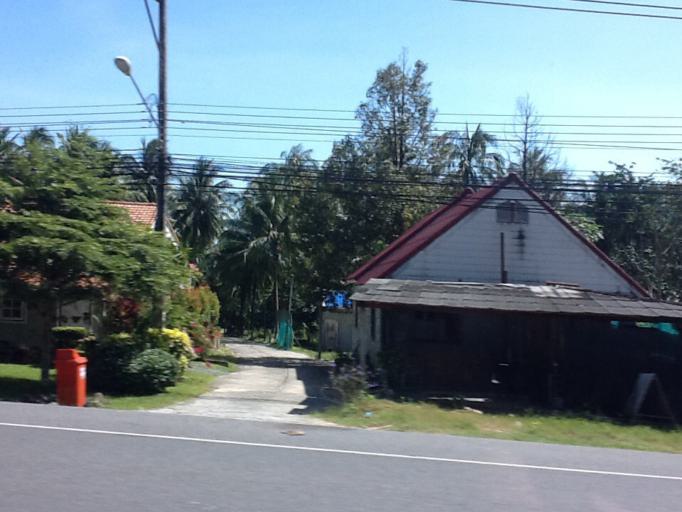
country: TH
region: Phuket
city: Thalang
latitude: 8.0022
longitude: 98.3927
